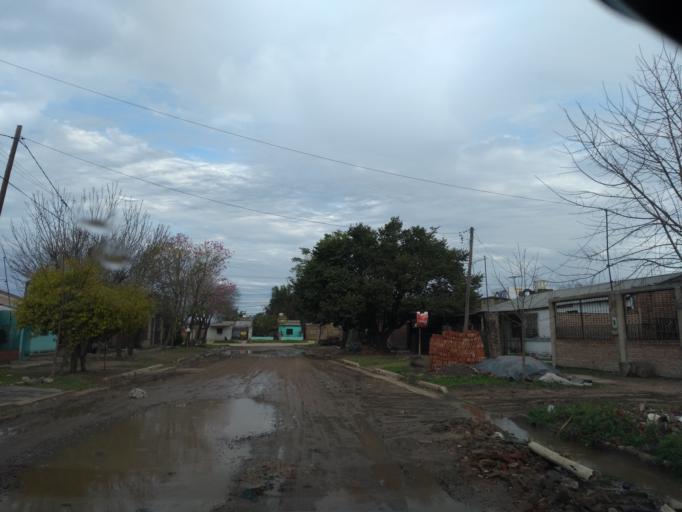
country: AR
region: Chaco
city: Resistencia
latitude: -27.4802
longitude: -58.9813
